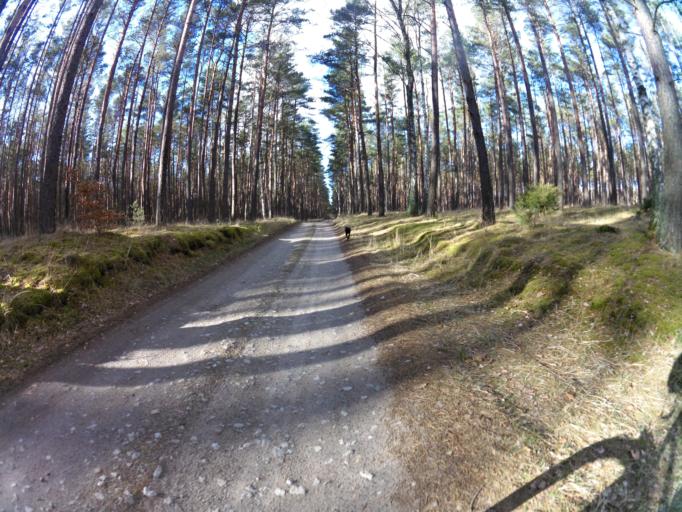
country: PL
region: West Pomeranian Voivodeship
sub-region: Powiat mysliborski
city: Debno
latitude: 52.7962
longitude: 14.7480
